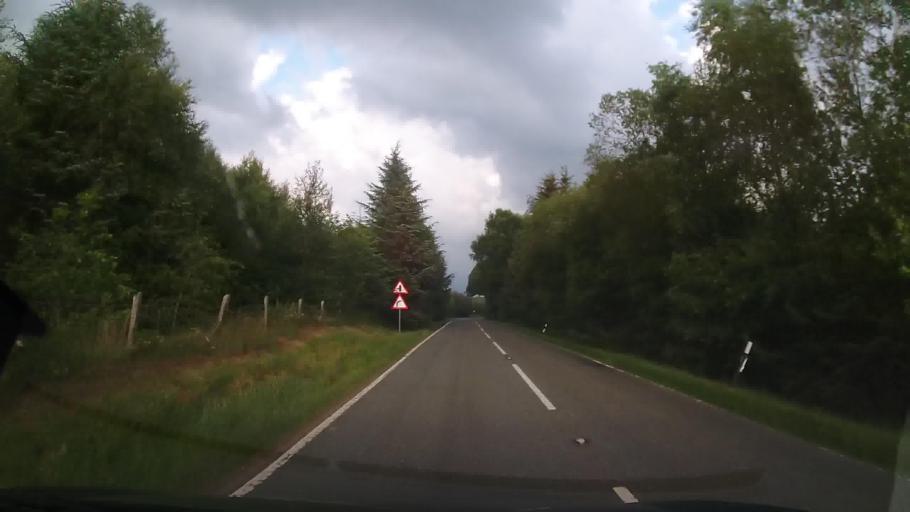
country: GB
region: Wales
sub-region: Denbighshire
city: Llandrillo
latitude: 52.9020
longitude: -3.5019
